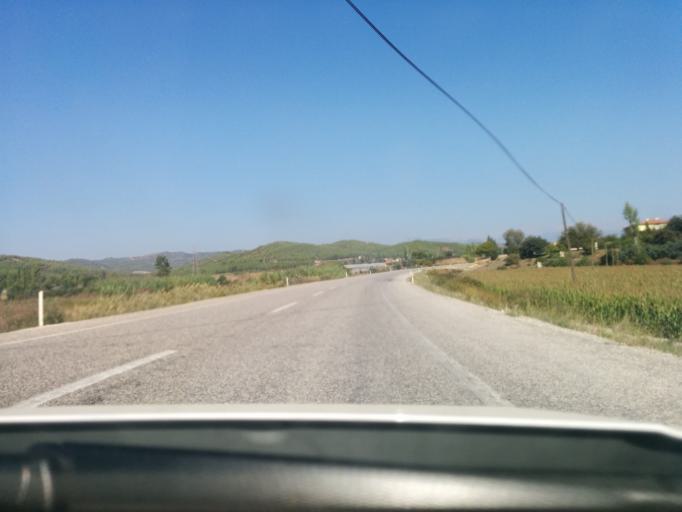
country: TR
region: Mugla
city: Kemer
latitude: 36.5644
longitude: 29.3459
